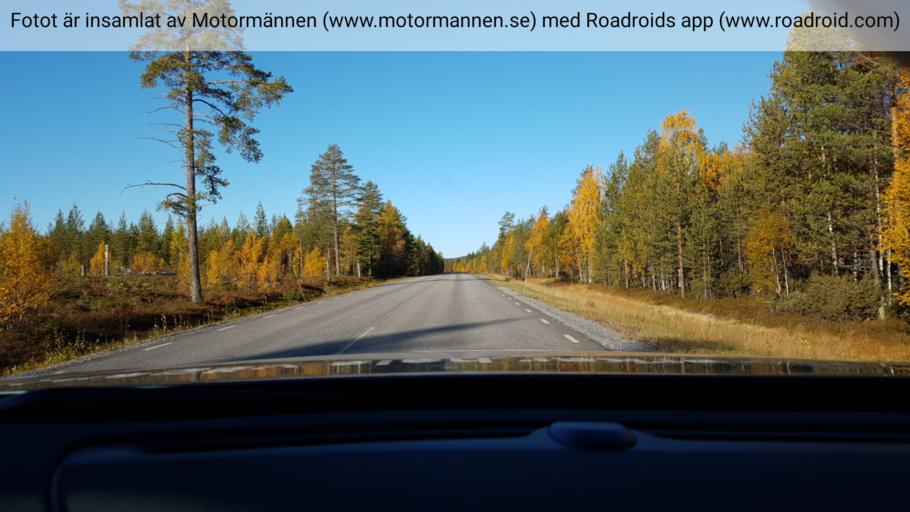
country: SE
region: Norrbotten
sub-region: Pitea Kommun
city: Roknas
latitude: 65.3418
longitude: 20.9684
